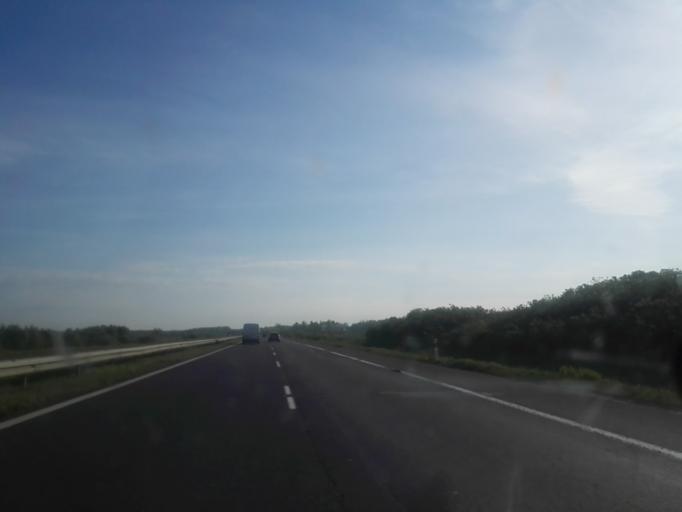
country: PL
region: Lodz Voivodeship
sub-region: Powiat radomszczanski
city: Kamiensk
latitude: 51.2251
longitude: 19.5050
